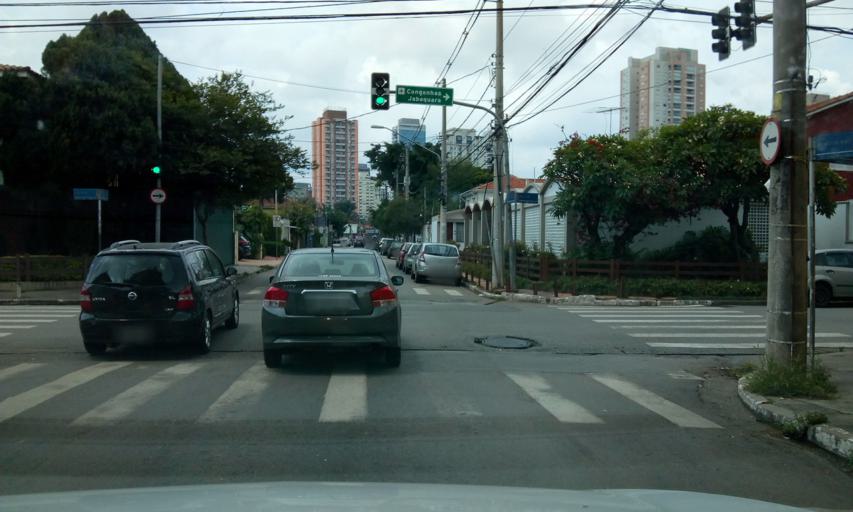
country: BR
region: Sao Paulo
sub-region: Sao Paulo
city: Sao Paulo
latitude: -23.6056
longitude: -46.6811
